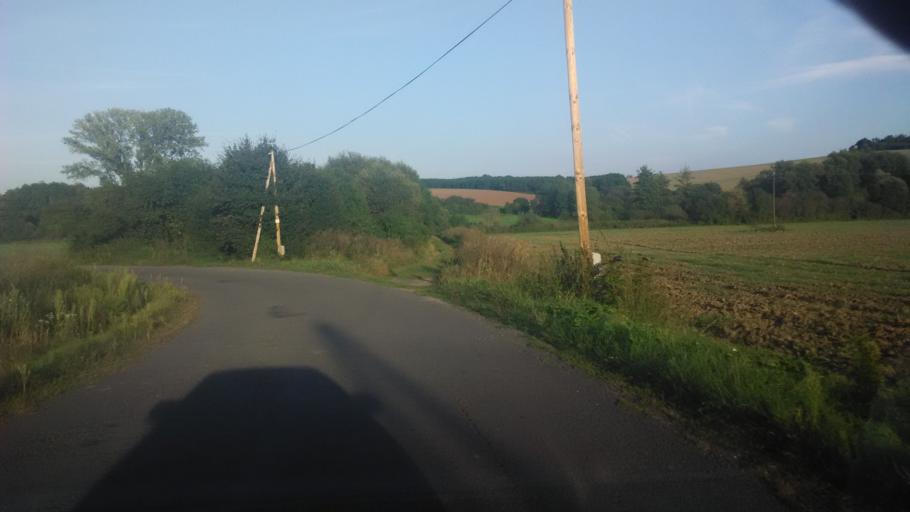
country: SK
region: Banskobystricky
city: Dudince
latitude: 48.1975
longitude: 18.8524
